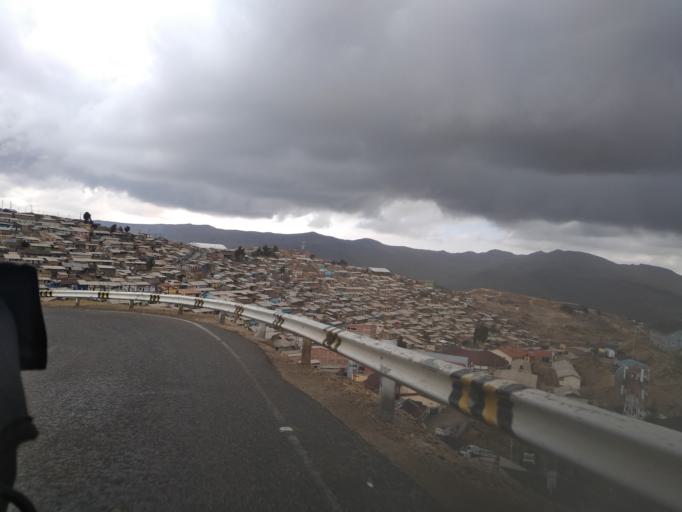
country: PE
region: La Libertad
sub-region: Provincia de Santiago de Chuco
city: Quiruvilca
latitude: -8.0001
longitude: -78.3091
